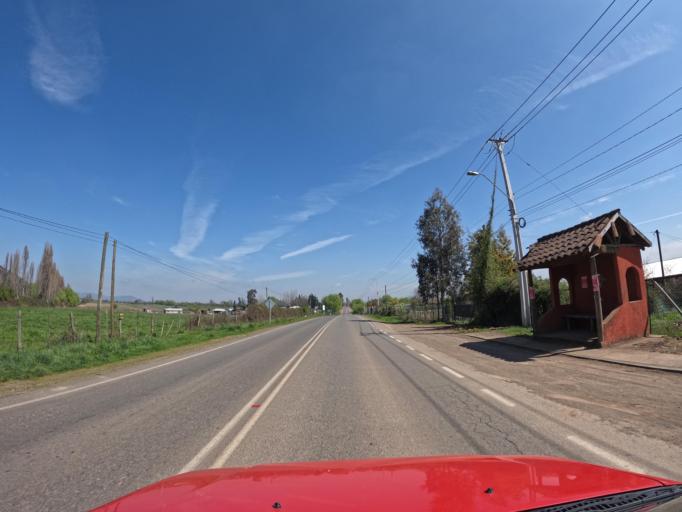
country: CL
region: Maule
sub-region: Provincia de Talca
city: San Clemente
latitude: -35.4914
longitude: -71.3062
